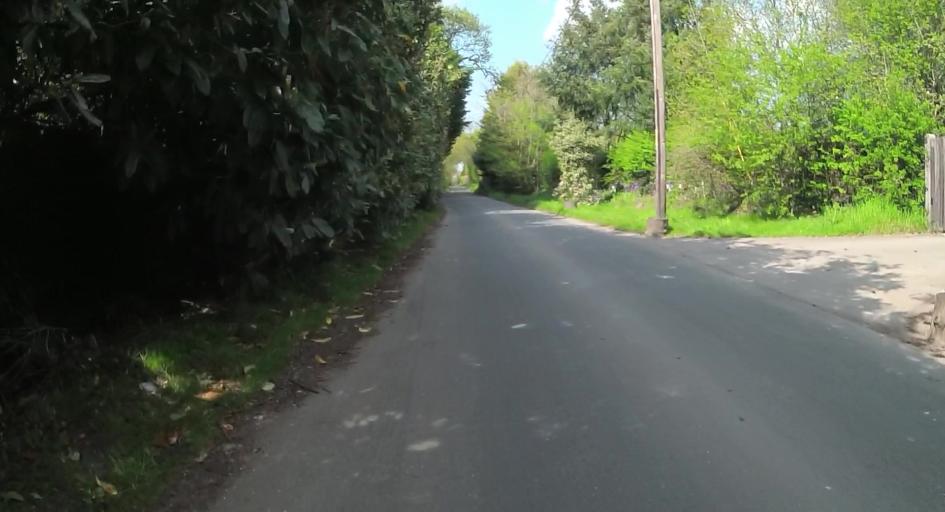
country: GB
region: England
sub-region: Hampshire
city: Tadley
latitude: 51.3780
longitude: -1.1268
